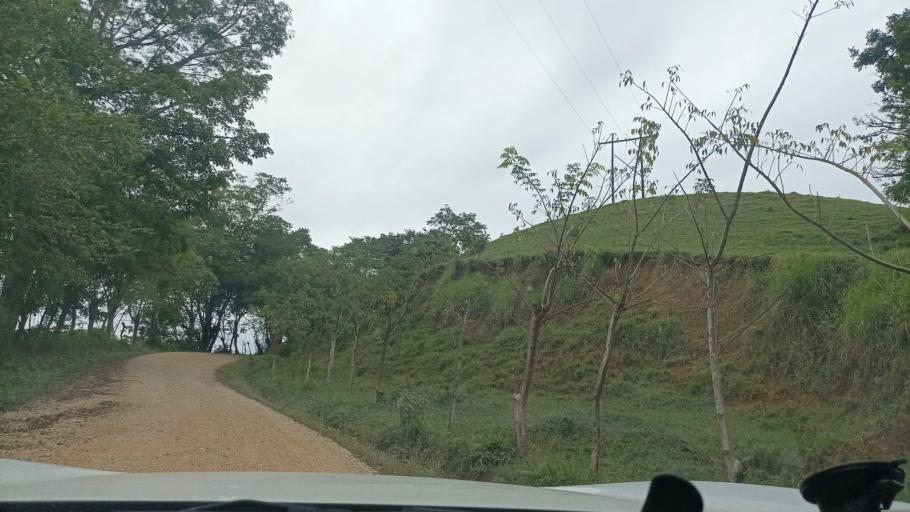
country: MX
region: Veracruz
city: Hidalgotitlan
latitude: 17.6070
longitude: -94.5250
